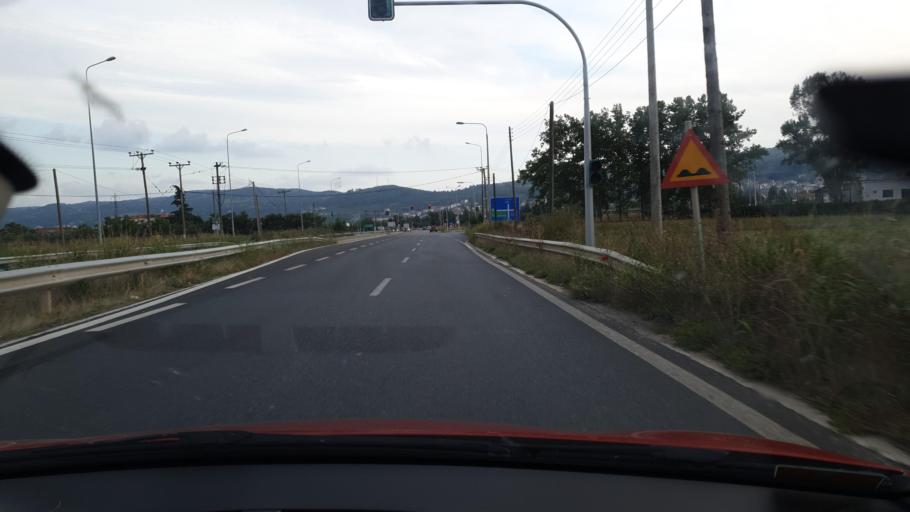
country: GR
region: Central Macedonia
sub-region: Nomos Thessalonikis
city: Liti
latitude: 40.7536
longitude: 22.9895
